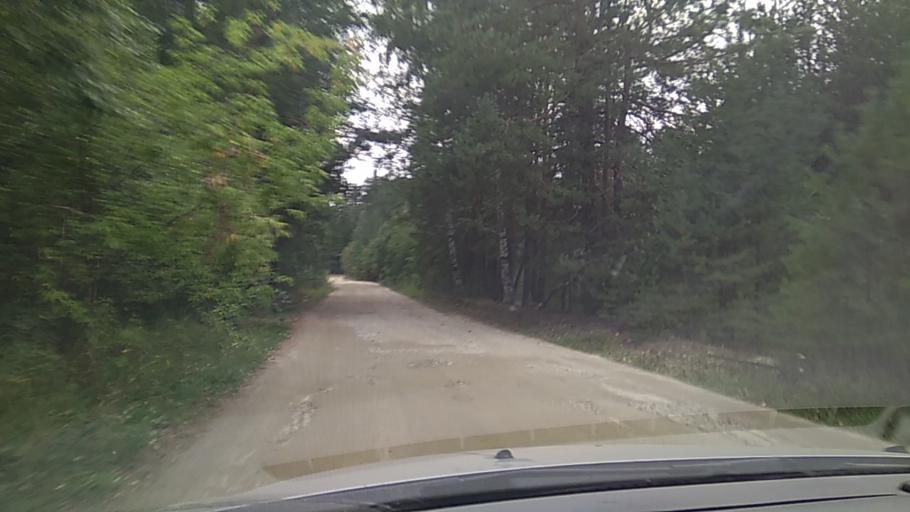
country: RU
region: Chelyabinsk
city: Kyshtym
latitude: 55.6799
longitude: 60.5773
